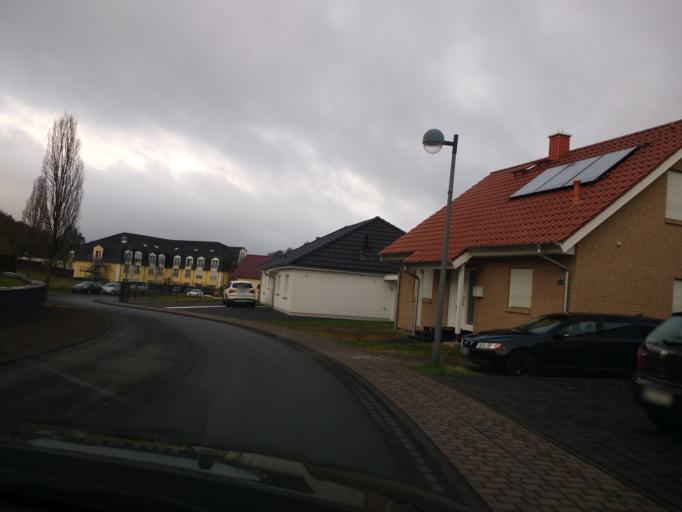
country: DE
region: Rheinland-Pfalz
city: Gerolstein
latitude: 50.2317
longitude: 6.6513
